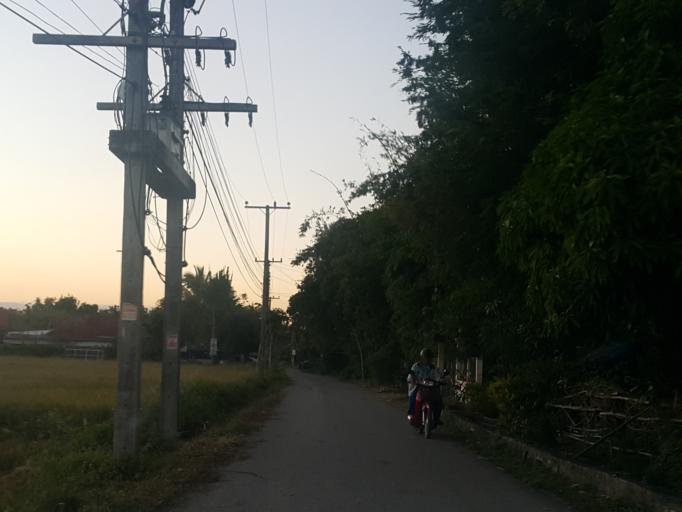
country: TH
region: Chiang Mai
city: San Kamphaeng
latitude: 18.8241
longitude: 99.1410
